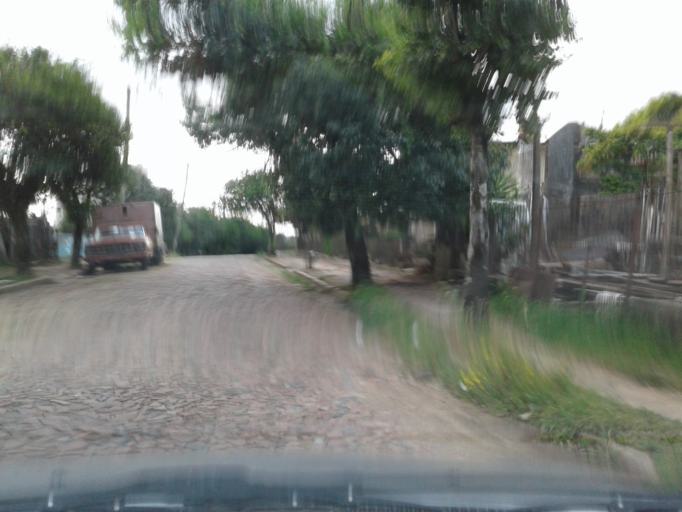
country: BR
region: Rio Grande do Sul
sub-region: Porto Alegre
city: Porto Alegre
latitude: -30.0646
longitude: -51.1483
